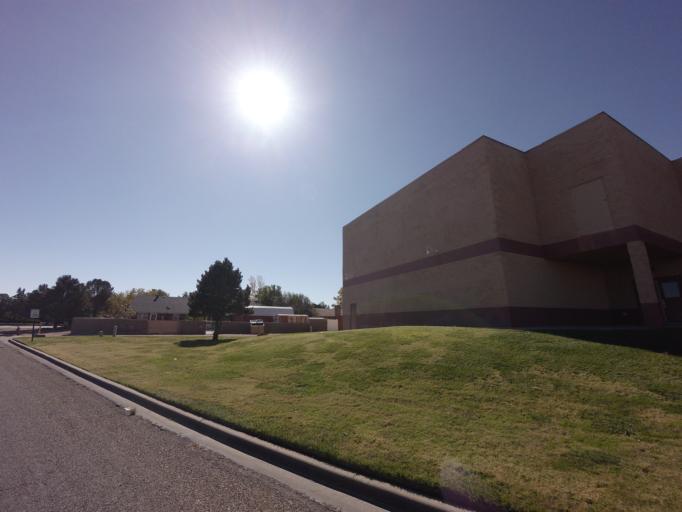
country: US
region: New Mexico
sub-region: Curry County
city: Clovis
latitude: 34.4241
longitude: -103.1907
